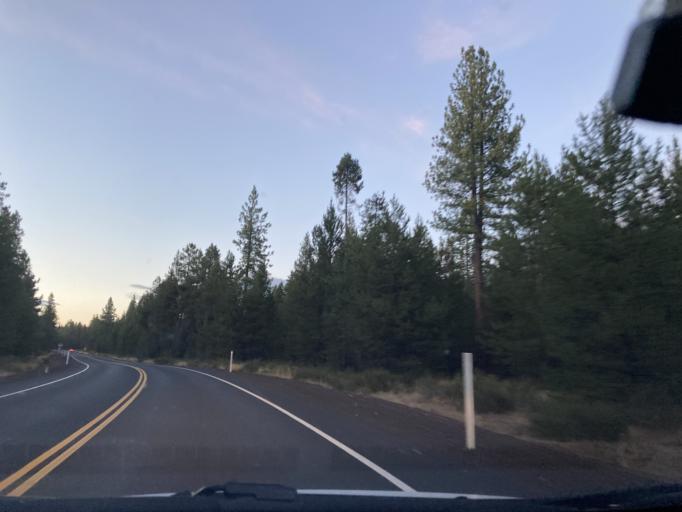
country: US
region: Oregon
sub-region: Deschutes County
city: Three Rivers
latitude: 43.8281
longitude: -121.4414
